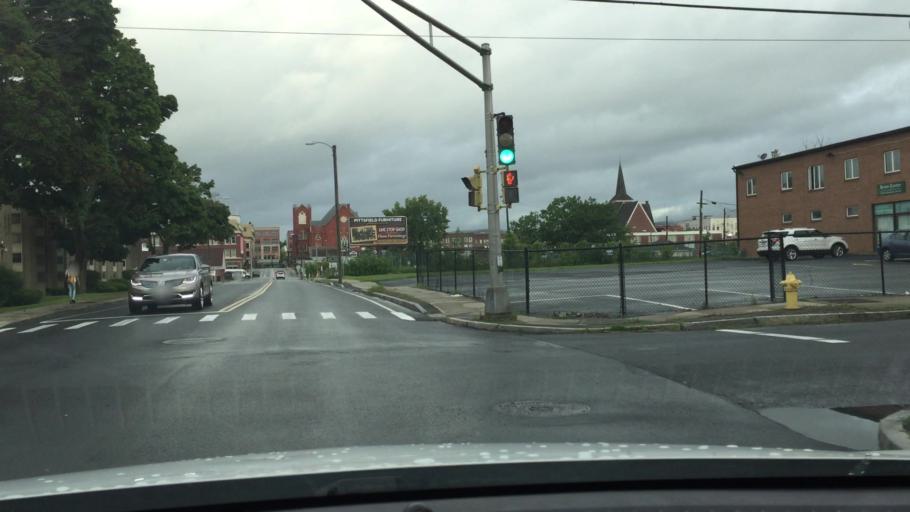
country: US
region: Massachusetts
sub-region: Berkshire County
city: Pittsfield
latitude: 42.4494
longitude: -73.2478
